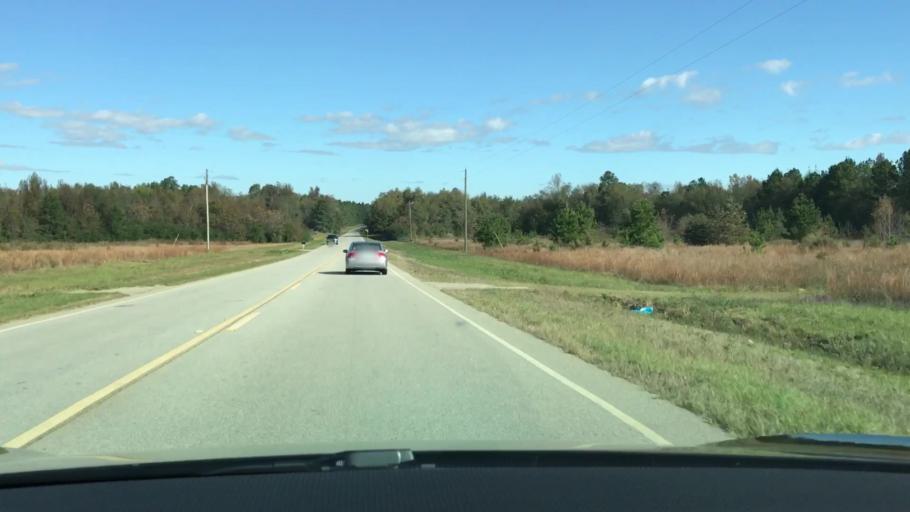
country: US
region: Georgia
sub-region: Jefferson County
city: Wrens
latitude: 33.2323
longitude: -82.4587
